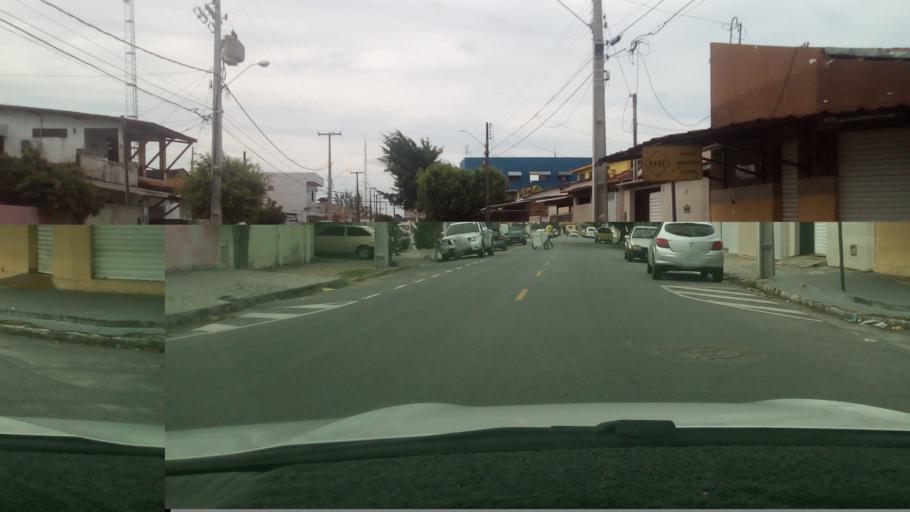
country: BR
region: Paraiba
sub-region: Joao Pessoa
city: Joao Pessoa
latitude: -7.1310
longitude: -34.8774
